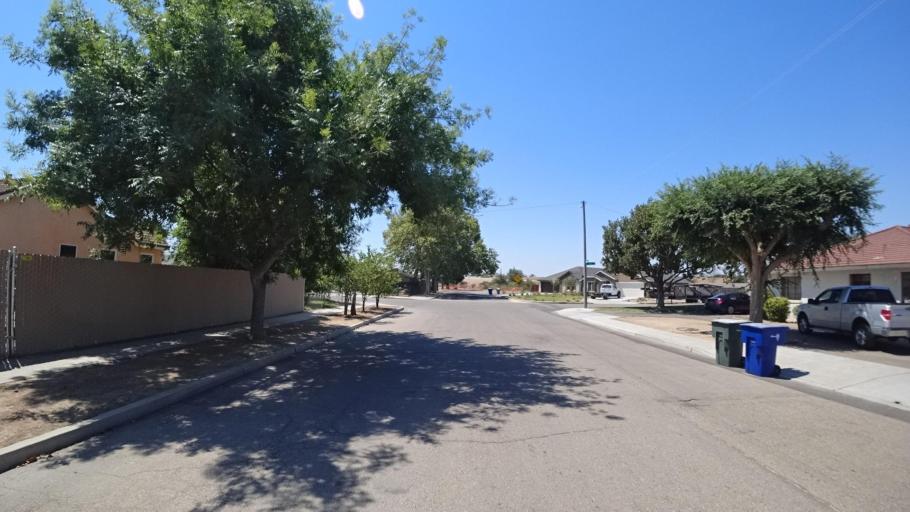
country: US
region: California
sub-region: Fresno County
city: Sunnyside
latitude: 36.7562
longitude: -119.7341
